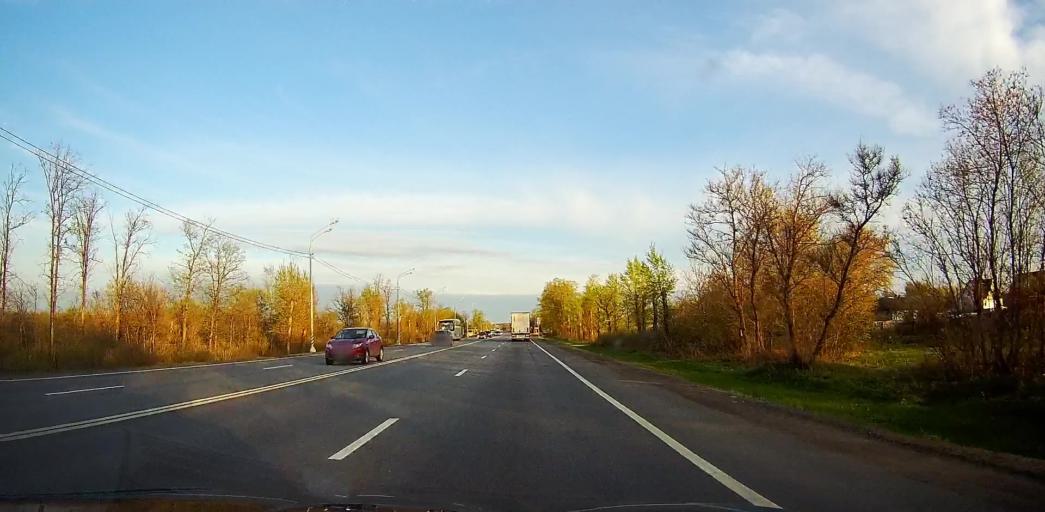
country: RU
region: Moskovskaya
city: Troitskoye
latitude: 55.2653
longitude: 38.5053
